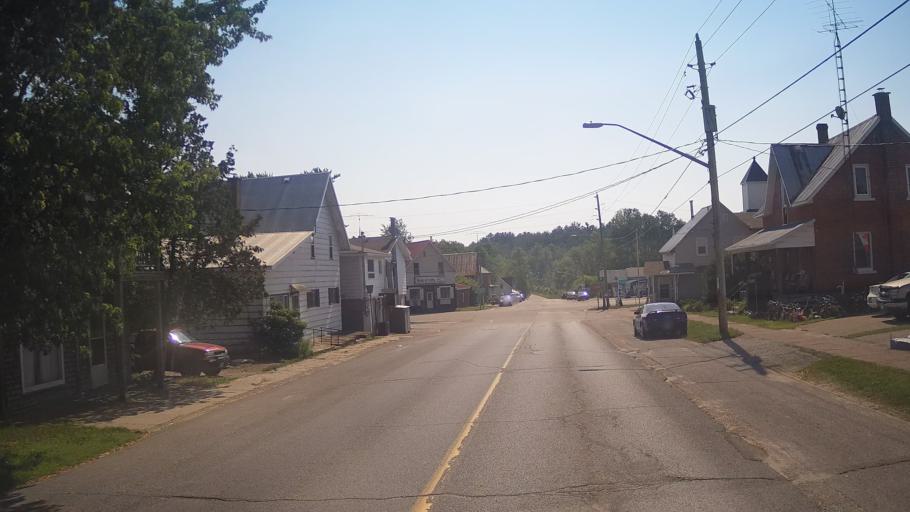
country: CA
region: Ontario
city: Pembroke
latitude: 45.5814
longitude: -77.2436
